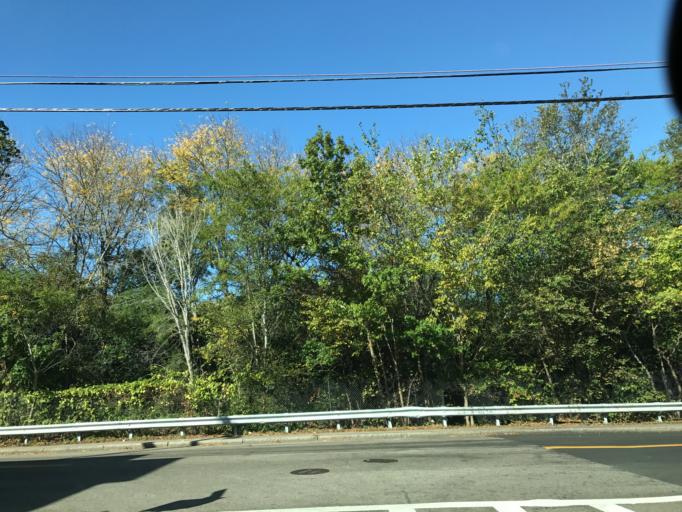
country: US
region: Massachusetts
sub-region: Suffolk County
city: Jamaica Plain
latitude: 42.2857
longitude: -71.0961
